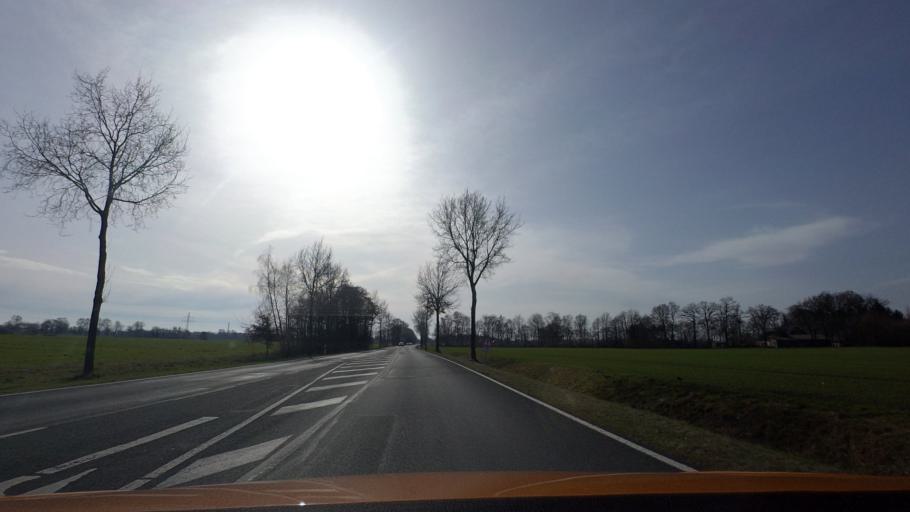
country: DE
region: Lower Saxony
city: Raddestorf
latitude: 52.4226
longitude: 8.9471
